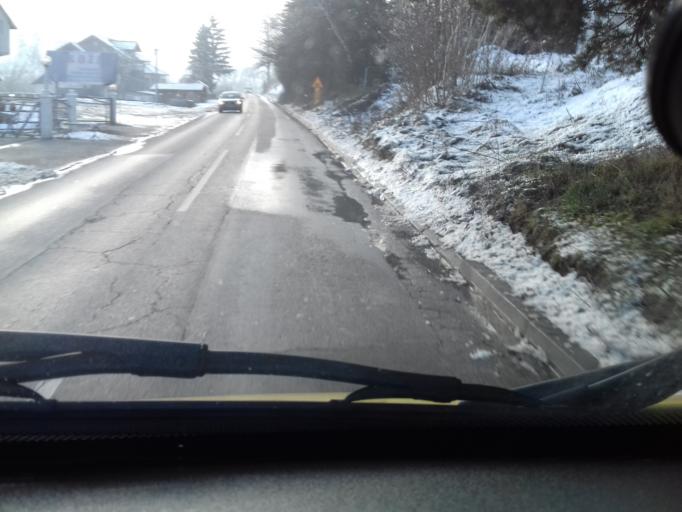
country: BA
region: Federation of Bosnia and Herzegovina
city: Visoko
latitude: 43.9946
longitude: 18.2049
